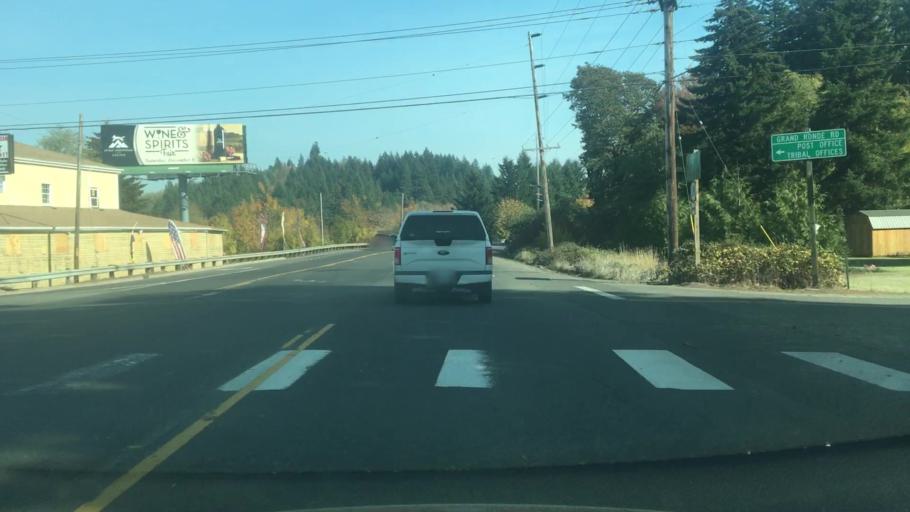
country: US
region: Oregon
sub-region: Polk County
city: Grand Ronde
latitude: 45.0592
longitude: -123.6095
